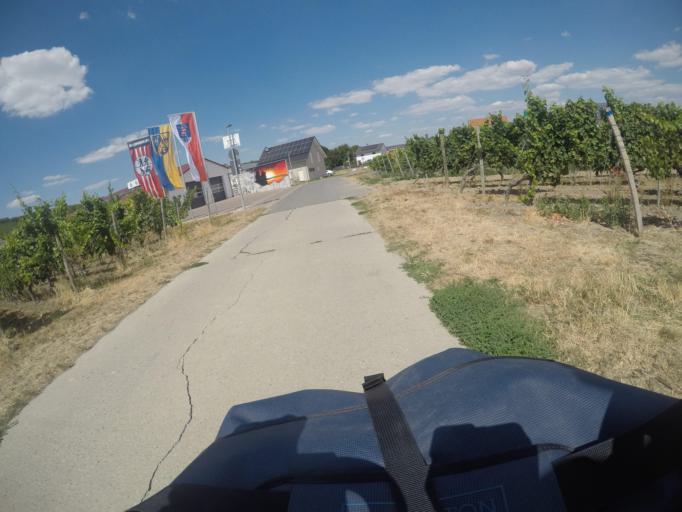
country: DE
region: Rheinland-Pfalz
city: Ludwigshohe
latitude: 49.8151
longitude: 8.3463
